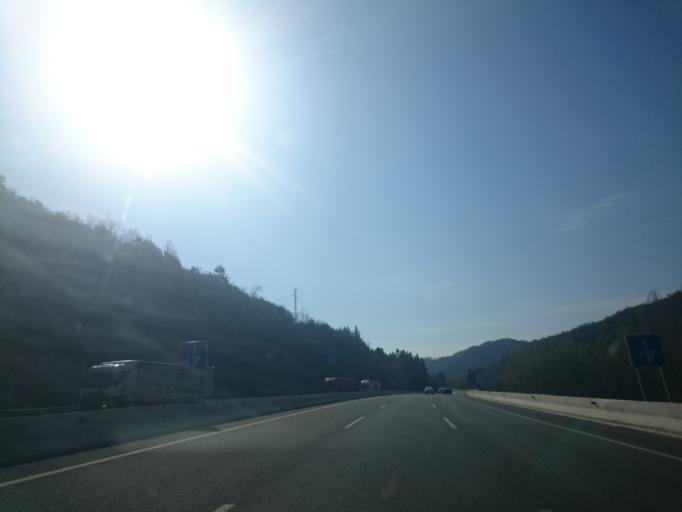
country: ES
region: Catalonia
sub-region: Provincia de Girona
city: Viladrau
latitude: 41.8792
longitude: 2.3986
